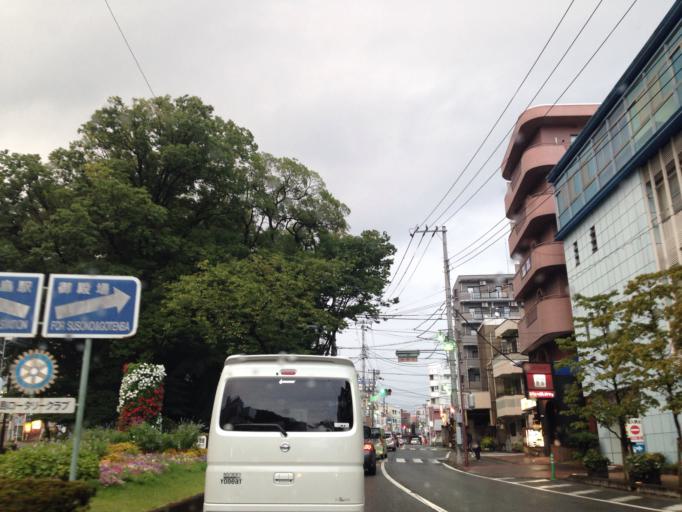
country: JP
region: Shizuoka
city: Mishima
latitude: 35.1238
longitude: 138.9140
